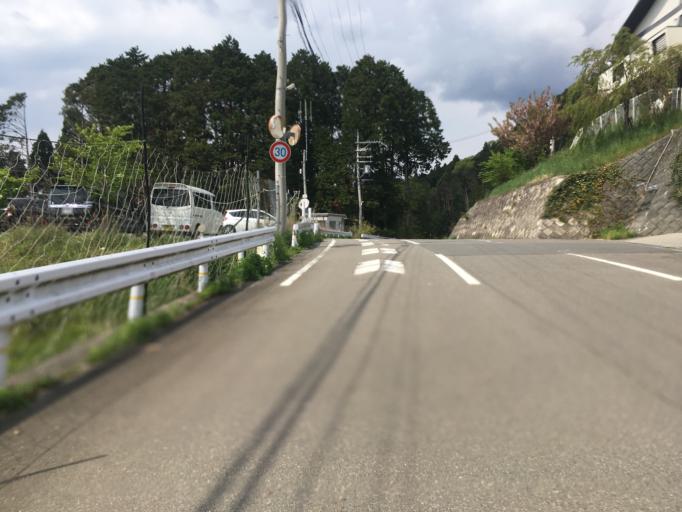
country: JP
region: Kyoto
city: Kameoka
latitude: 35.0763
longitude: 135.6112
